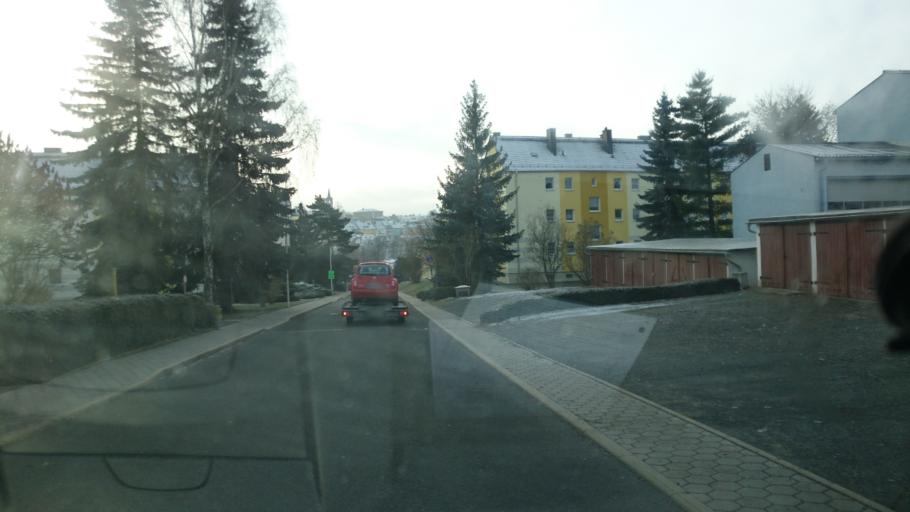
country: DE
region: Thuringia
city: Schleiz
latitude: 50.5841
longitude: 11.8115
